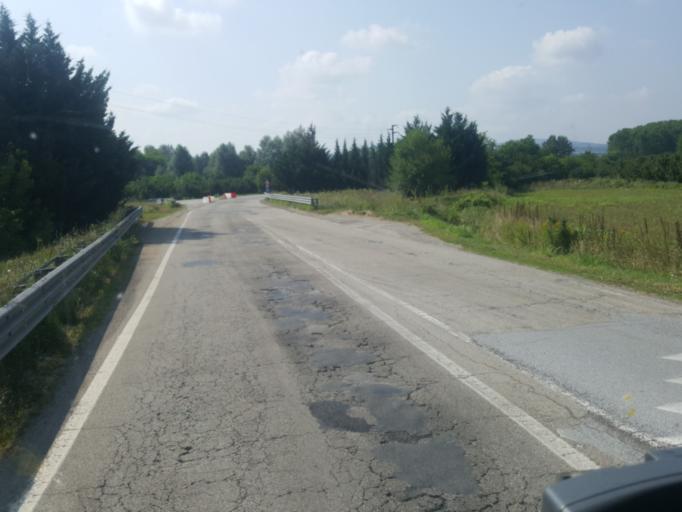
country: IT
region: Piedmont
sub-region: Provincia di Cuneo
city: Roddi
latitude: 44.6777
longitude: 7.9843
